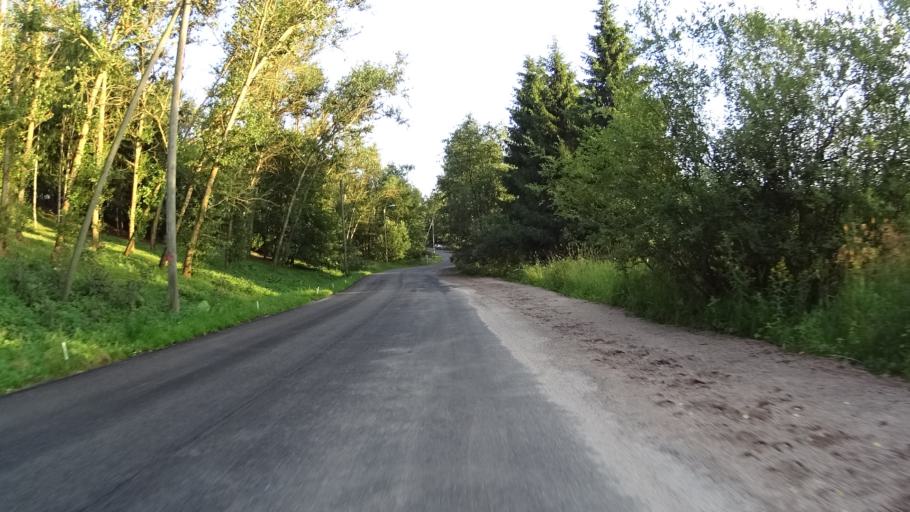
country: FI
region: Uusimaa
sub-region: Helsinki
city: Teekkarikylae
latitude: 60.2156
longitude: 24.8466
